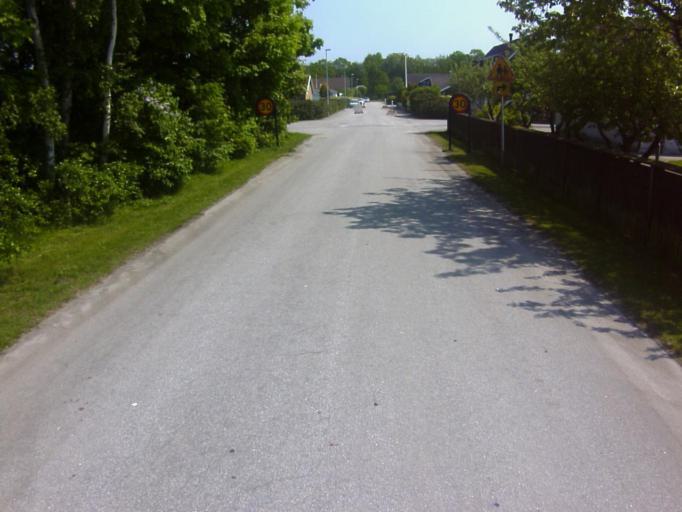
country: SE
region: Blekinge
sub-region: Karlshamns Kommun
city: Morrum
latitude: 56.1274
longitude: 14.6688
